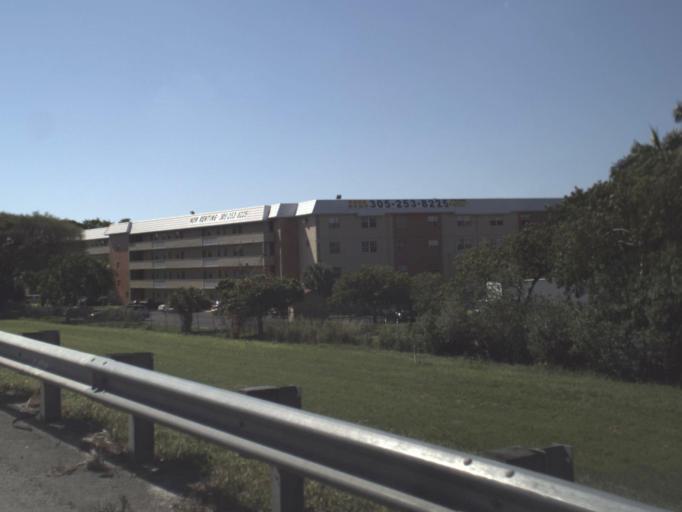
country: US
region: Florida
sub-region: Miami-Dade County
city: South Miami Heights
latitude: 25.5854
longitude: -80.3677
